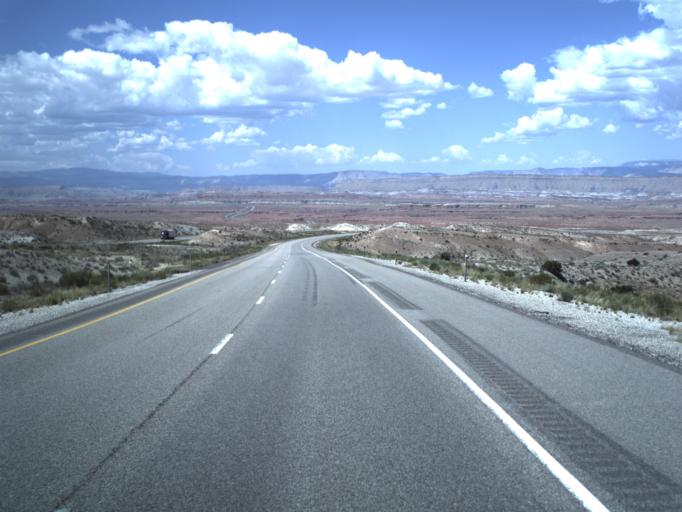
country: US
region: Utah
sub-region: Emery County
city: Ferron
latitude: 38.8441
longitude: -110.9764
